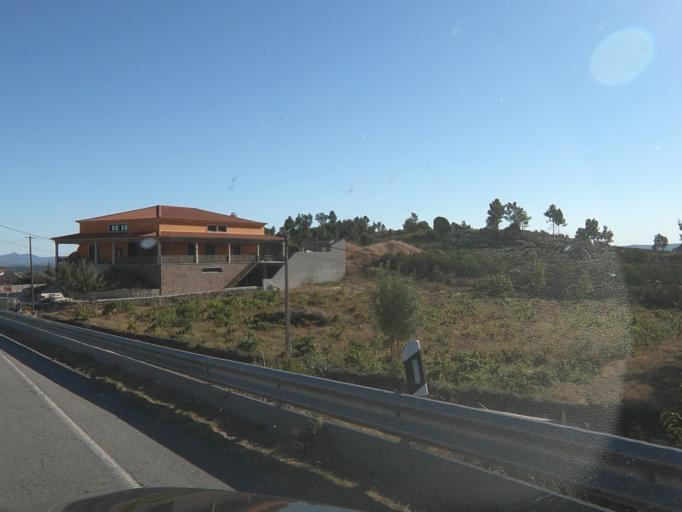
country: PT
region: Vila Real
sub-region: Valpacos
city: Valpacos
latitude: 41.6317
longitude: -7.3175
